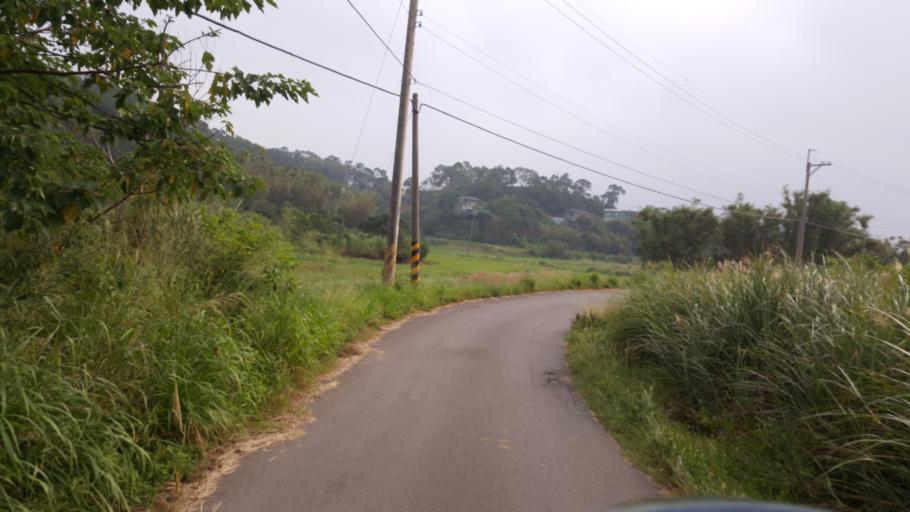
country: TW
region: Taiwan
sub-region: Hsinchu
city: Hsinchu
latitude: 24.7079
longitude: 120.9459
